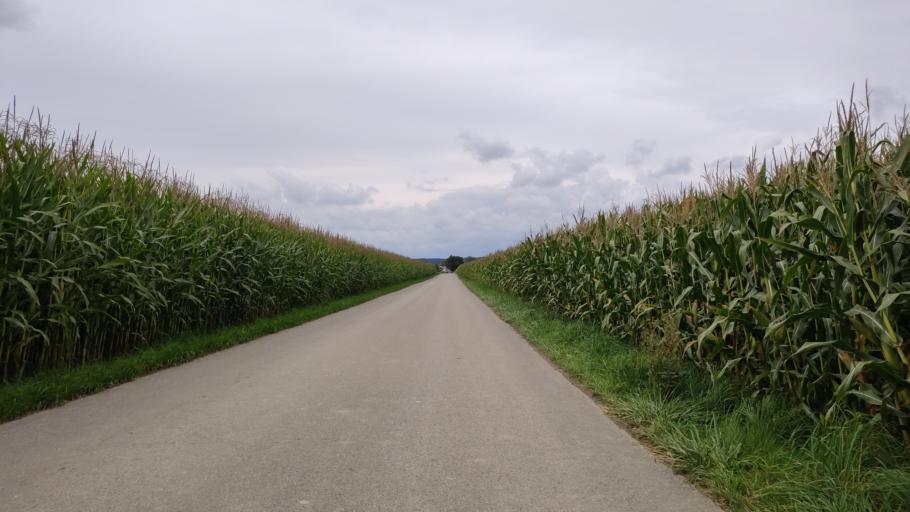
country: DE
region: Bavaria
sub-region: Swabia
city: Wehringen
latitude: 48.2401
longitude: 10.8113
